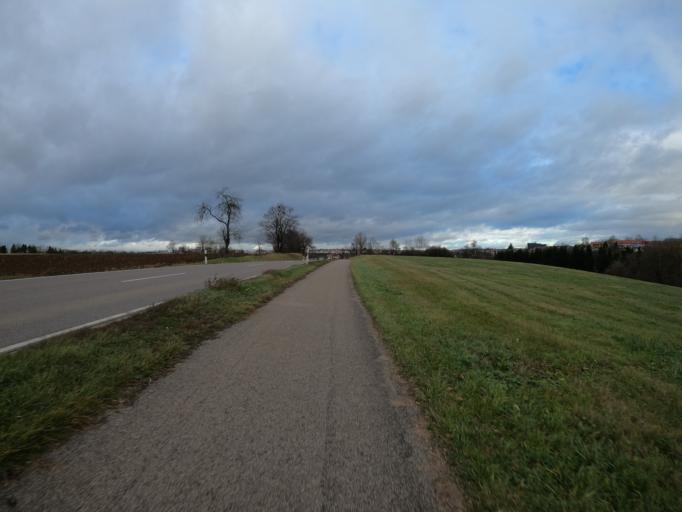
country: DE
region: Baden-Wuerttemberg
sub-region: Regierungsbezirk Stuttgart
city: Waldstetten
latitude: 48.7790
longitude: 9.8384
